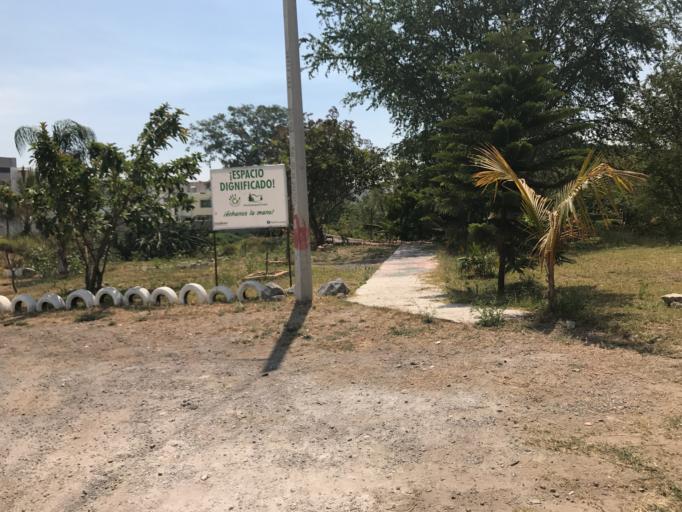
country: MX
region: Nayarit
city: Tepic
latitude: 21.5134
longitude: -104.9127
